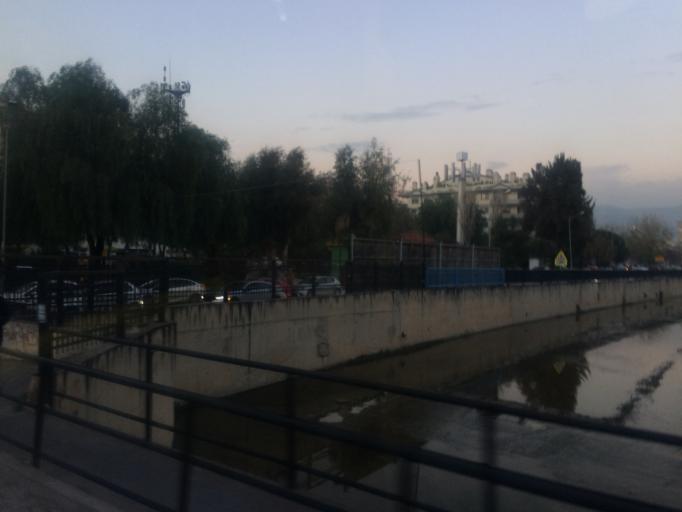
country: TR
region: Izmir
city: Karsiyaka
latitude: 38.4607
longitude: 27.0960
